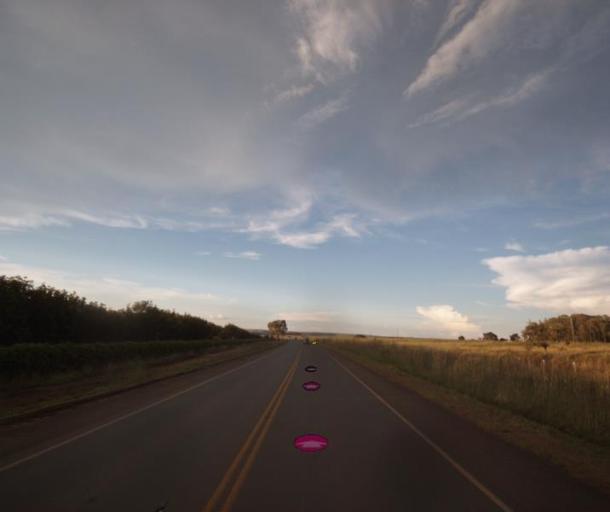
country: BR
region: Goias
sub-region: Anapolis
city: Anapolis
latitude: -16.2001
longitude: -48.9099
